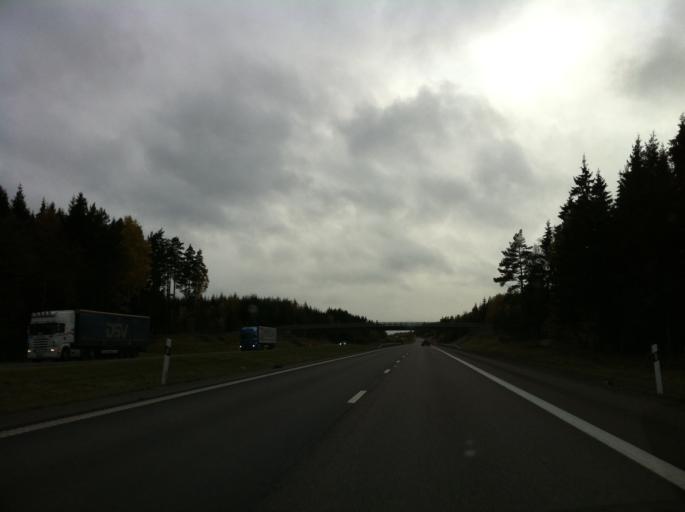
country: SE
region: OEstergoetland
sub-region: Odeshogs Kommun
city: OEdeshoeg
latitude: 58.2464
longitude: 14.7680
